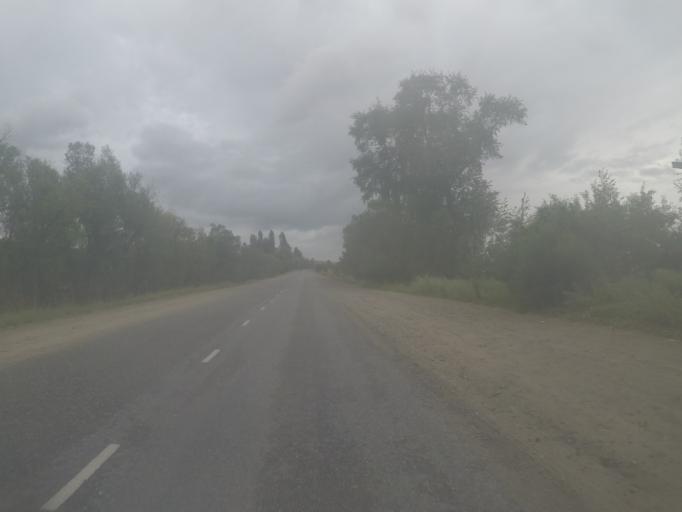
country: KG
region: Ysyk-Koel
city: Tyup
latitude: 42.6853
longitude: 78.3608
